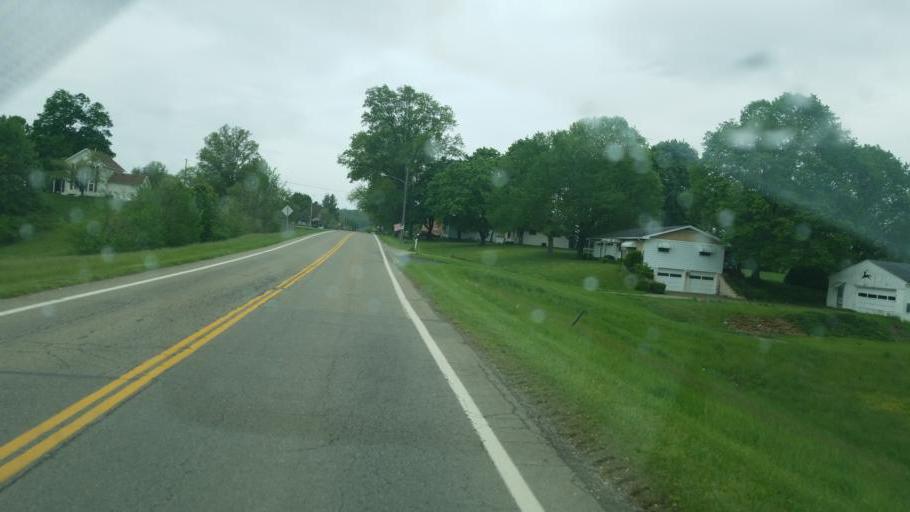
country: US
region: Ohio
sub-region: Coshocton County
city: West Lafayette
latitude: 40.2083
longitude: -81.7148
